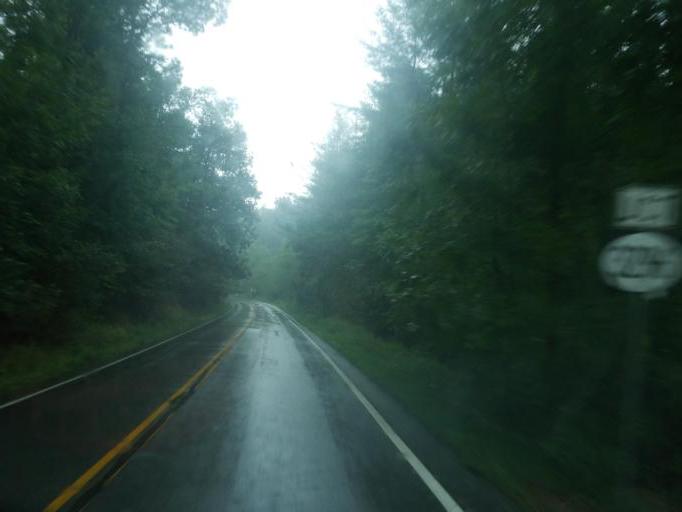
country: US
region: Kentucky
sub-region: Rowan County
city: Morehead
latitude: 38.2722
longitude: -83.3172
